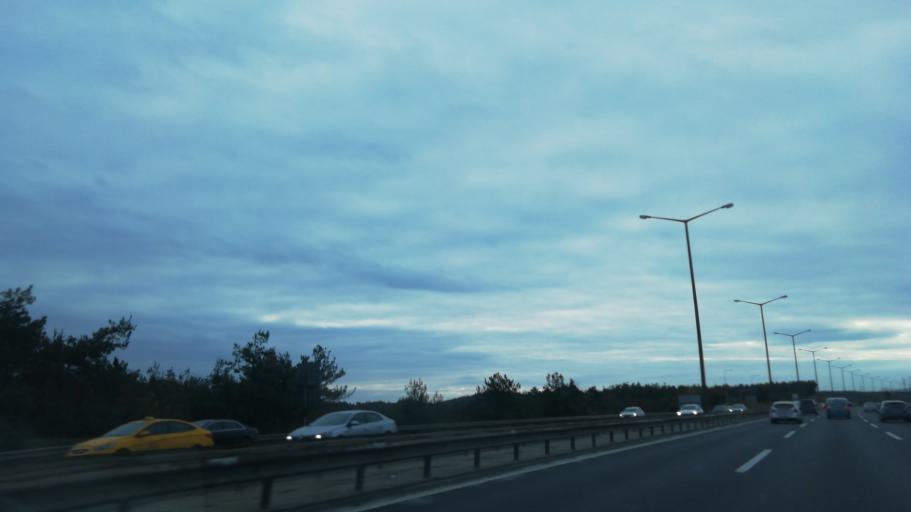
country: TR
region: Istanbul
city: Umraniye
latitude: 41.0598
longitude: 29.1166
